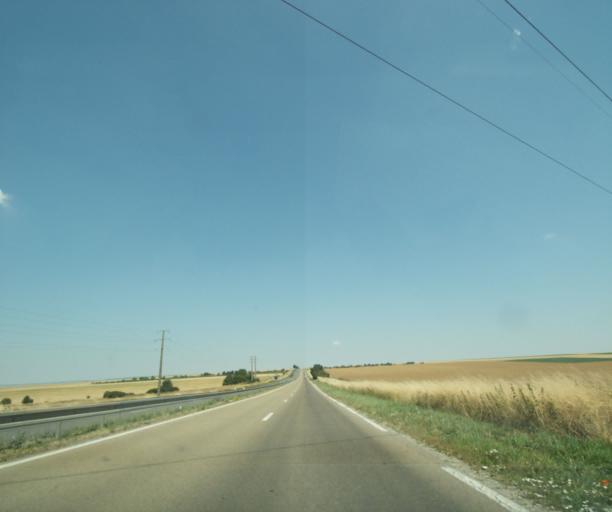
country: FR
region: Champagne-Ardenne
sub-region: Departement de la Marne
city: Fagnieres
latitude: 48.9996
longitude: 4.3389
